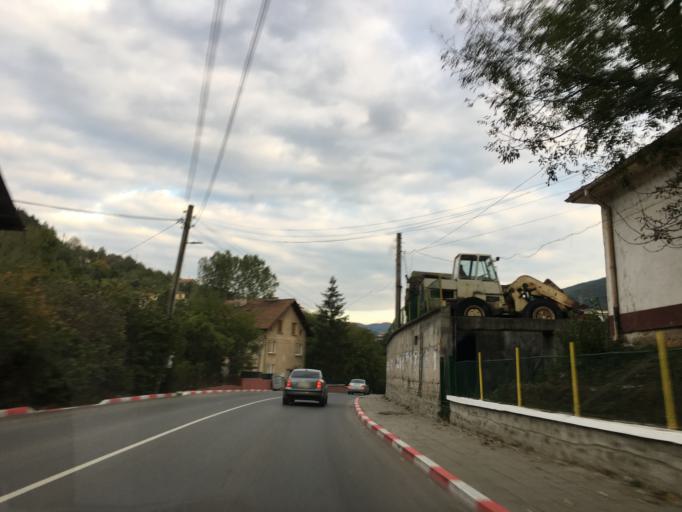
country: BG
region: Sofiya
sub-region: Obshtina Svoge
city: Svoge
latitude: 42.9602
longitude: 23.3530
